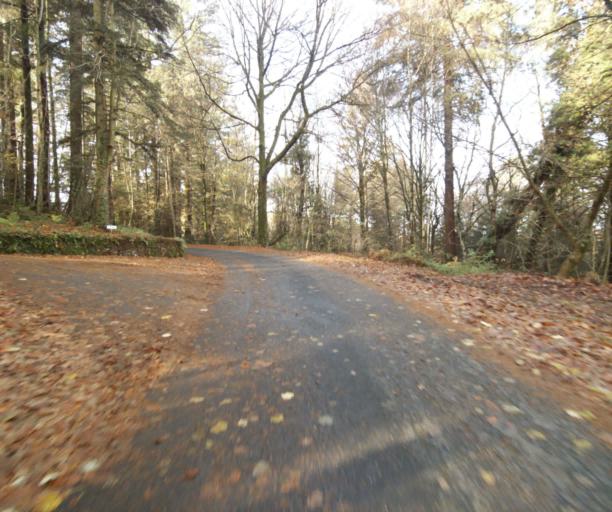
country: FR
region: Limousin
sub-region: Departement de la Correze
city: Sainte-Fortunade
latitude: 45.2161
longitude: 1.7437
